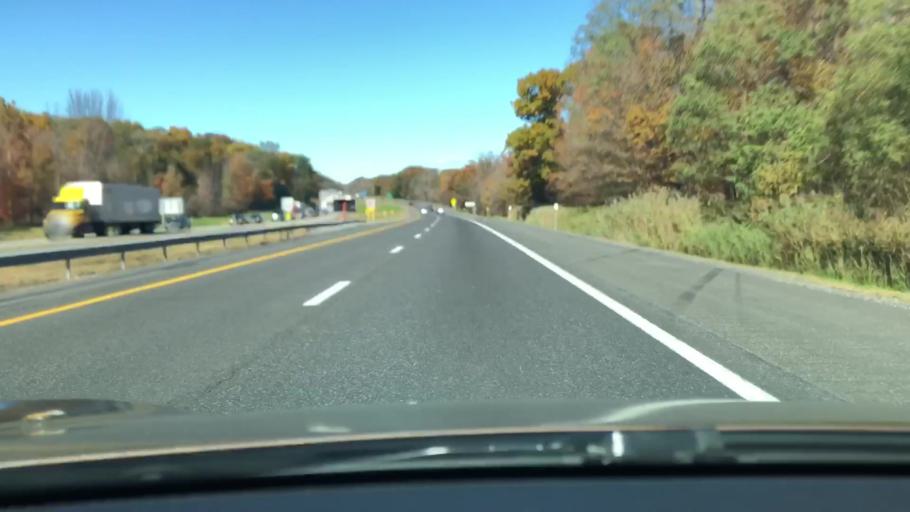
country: US
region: New York
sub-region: Orange County
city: Gardnertown
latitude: 41.5352
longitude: -74.0760
